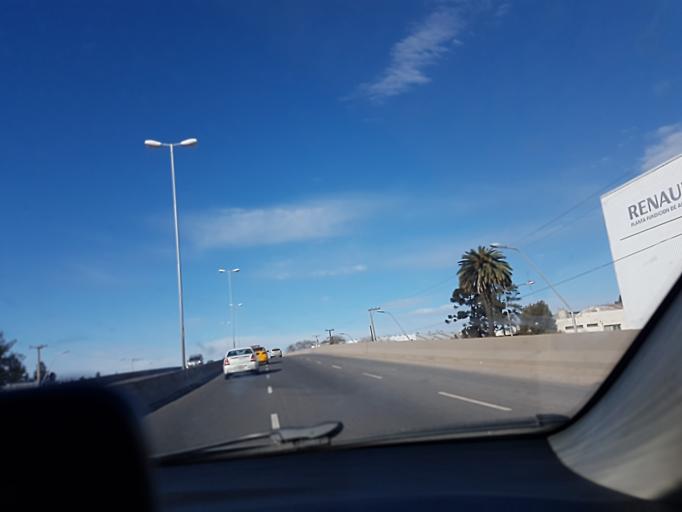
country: AR
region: Cordoba
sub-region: Departamento de Capital
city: Cordoba
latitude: -31.3418
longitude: -64.2080
